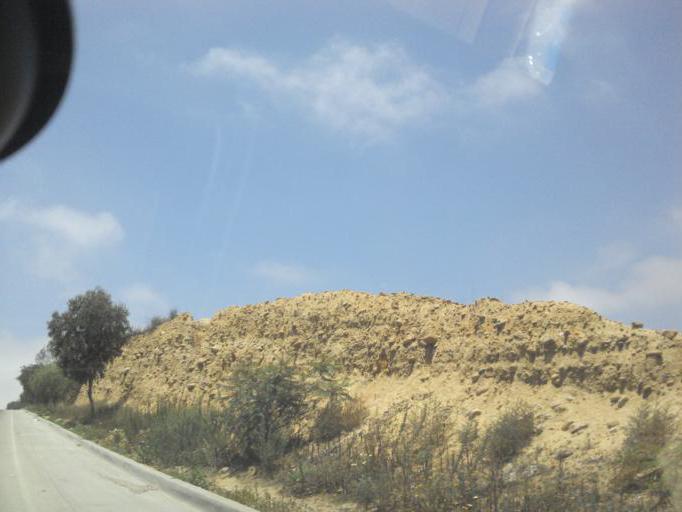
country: US
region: California
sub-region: San Diego County
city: Imperial Beach
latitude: 32.5387
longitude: -117.0721
